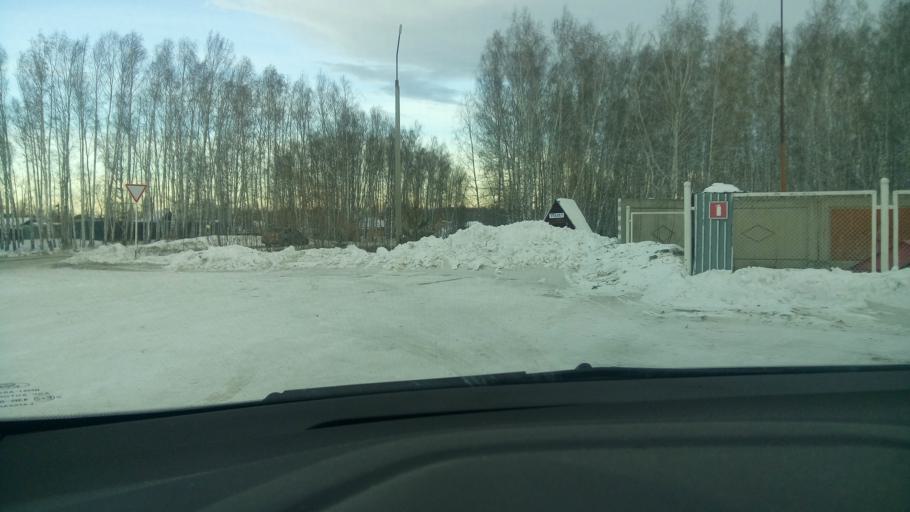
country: RU
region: Chelyabinsk
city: Ozersk
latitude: 55.7779
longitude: 60.7529
